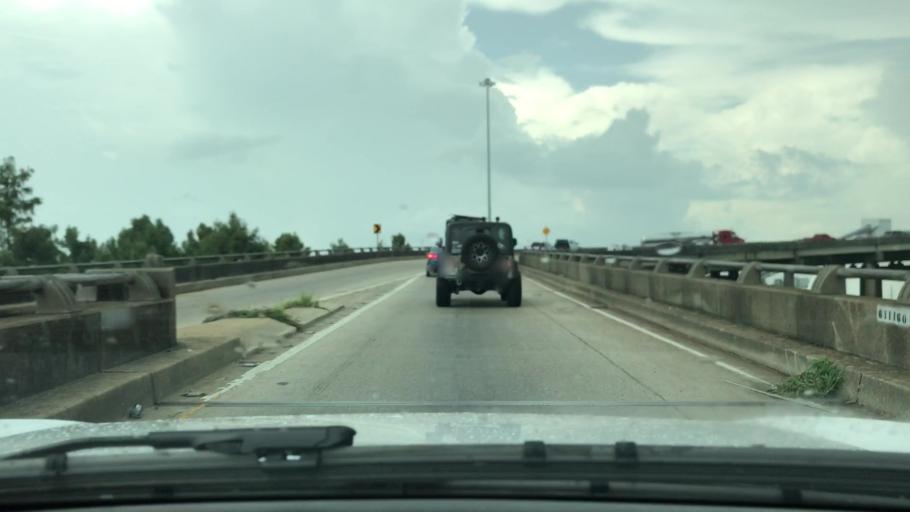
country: US
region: Louisiana
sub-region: West Baton Rouge Parish
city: Port Allen
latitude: 30.4388
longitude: -91.2079
